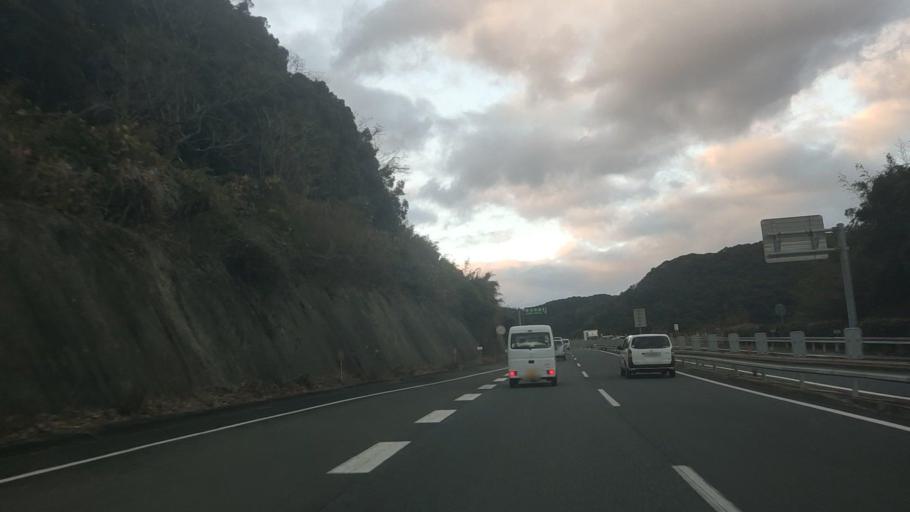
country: JP
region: Nagasaki
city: Obita
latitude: 32.8141
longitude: 129.9566
